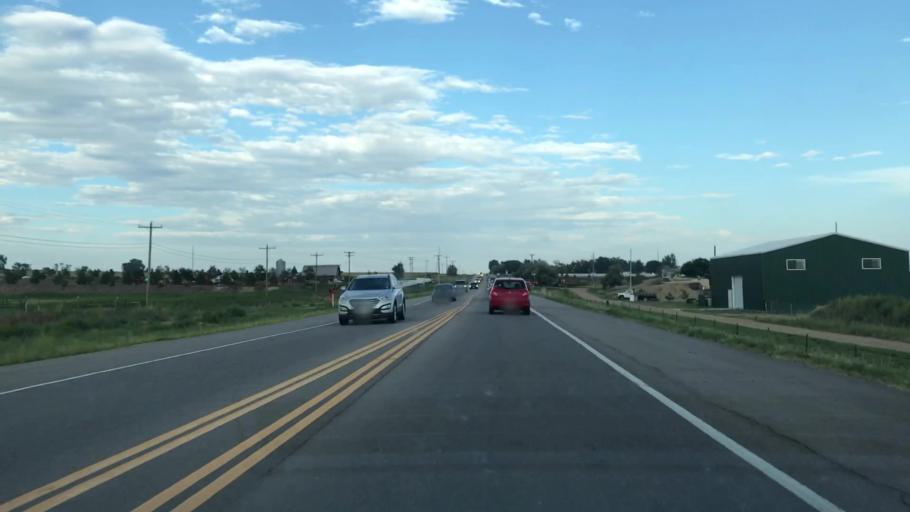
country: US
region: Colorado
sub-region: Weld County
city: Mead
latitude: 40.2035
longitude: -105.0502
